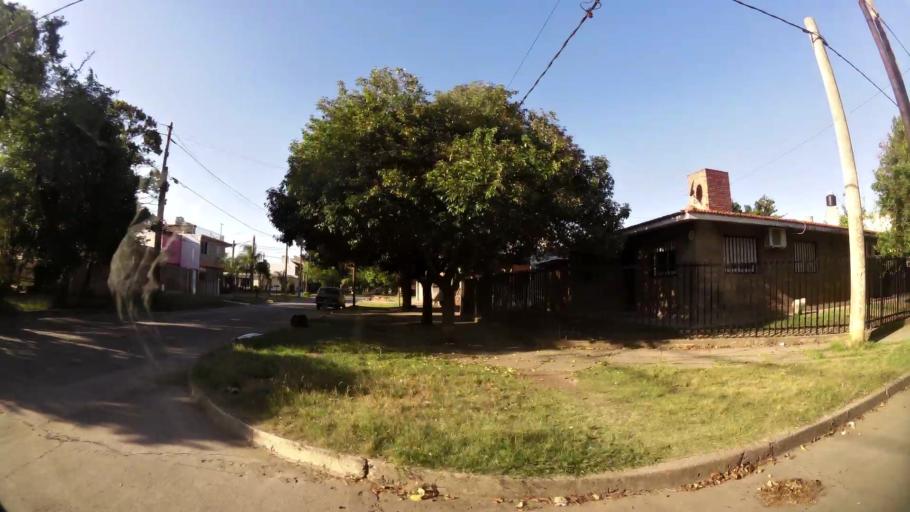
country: AR
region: Cordoba
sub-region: Departamento de Capital
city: Cordoba
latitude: -31.3787
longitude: -64.1810
